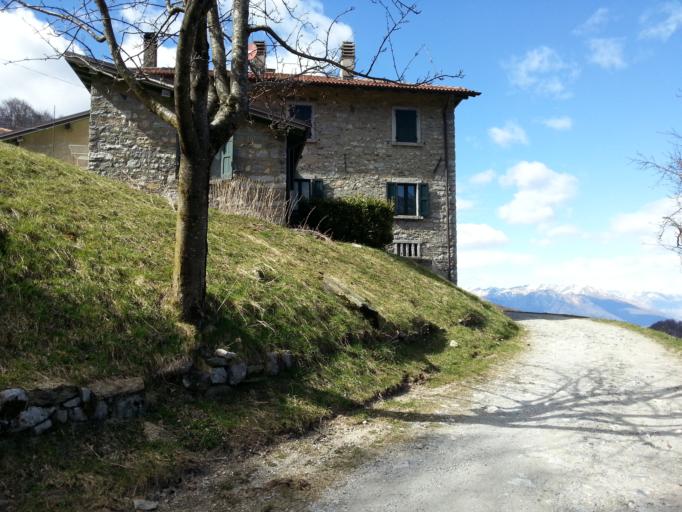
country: IT
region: Lombardy
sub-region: Provincia di Como
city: Lezzeno
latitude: 45.9242
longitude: 9.2211
